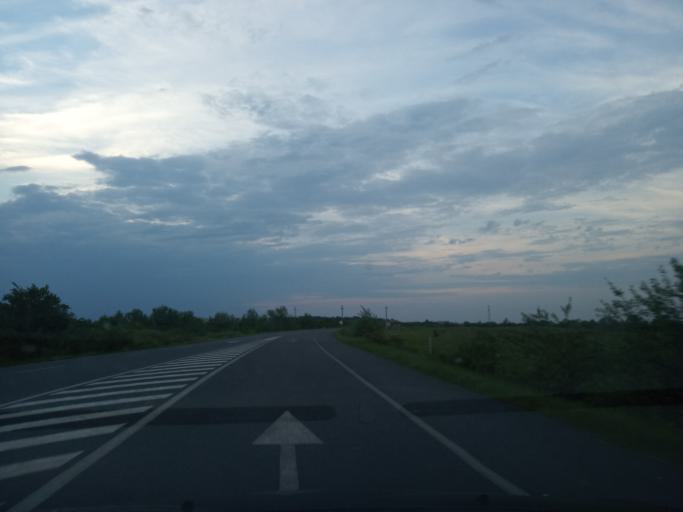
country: RO
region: Timis
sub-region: Oras Deta
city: Deta
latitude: 45.3746
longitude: 21.2341
